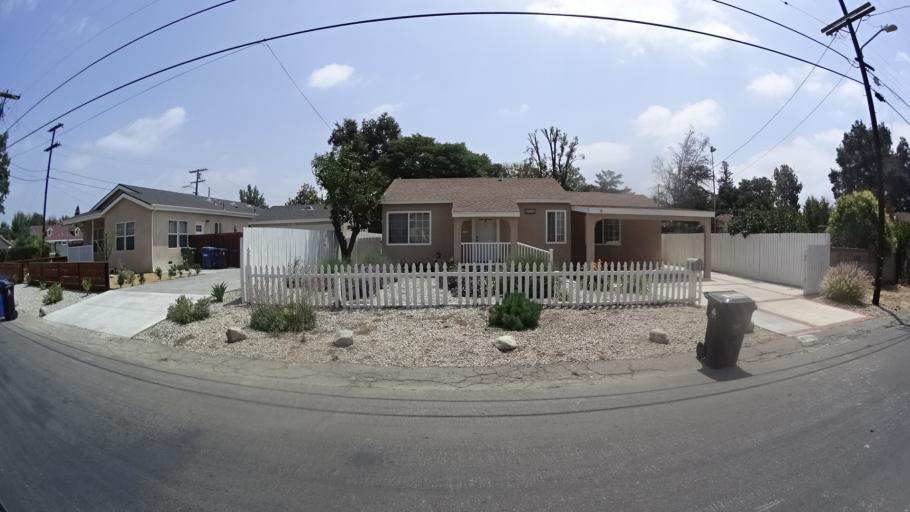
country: US
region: California
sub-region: Los Angeles County
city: Van Nuys
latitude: 34.1890
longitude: -118.4641
